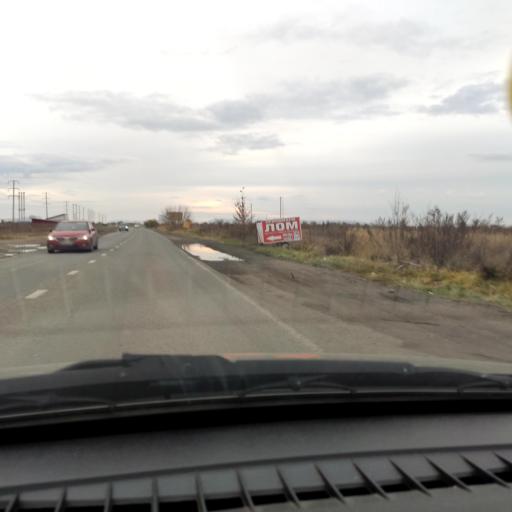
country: RU
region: Samara
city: Podstepki
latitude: 53.5232
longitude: 49.1973
